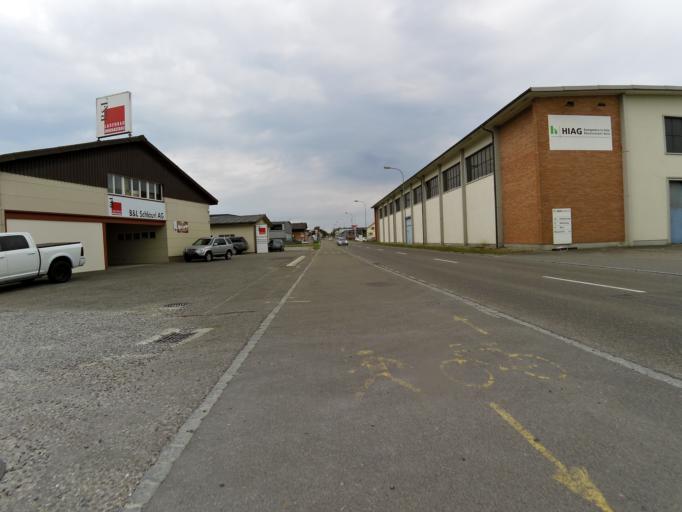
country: CH
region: Thurgau
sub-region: Kreuzlingen District
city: Ermatingen
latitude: 47.6663
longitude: 9.0914
